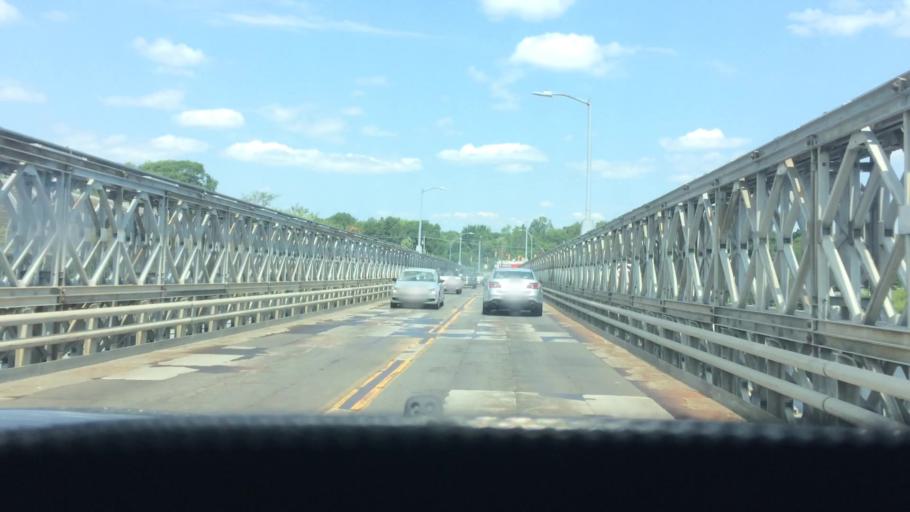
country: US
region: Massachusetts
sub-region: Middlesex County
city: Chelmsford
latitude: 42.6377
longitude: -71.3565
